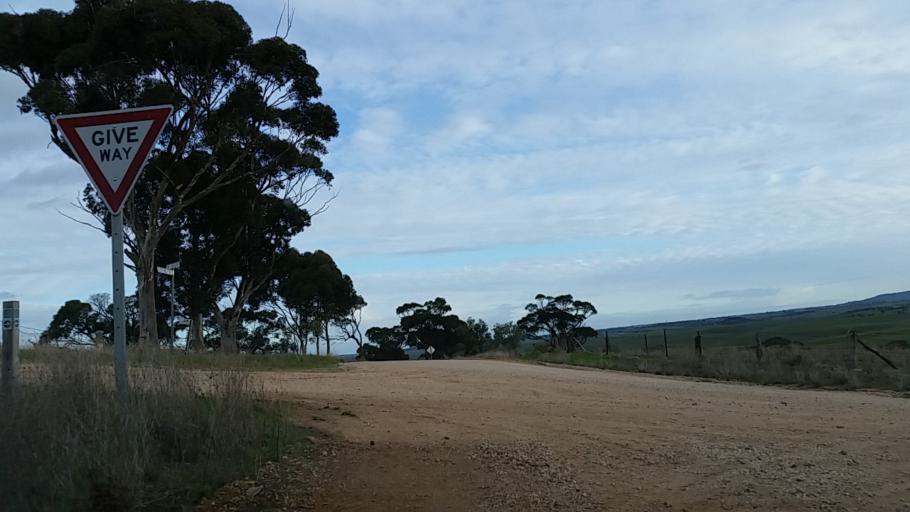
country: AU
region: South Australia
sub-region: Mount Barker
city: Callington
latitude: -35.0010
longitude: 139.0496
